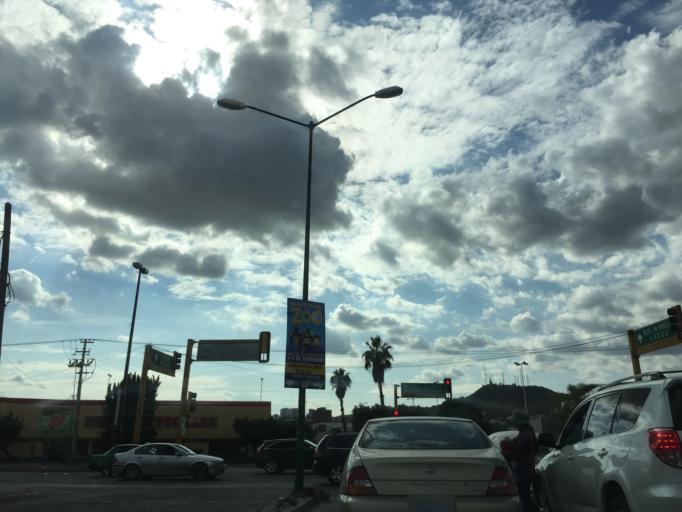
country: MX
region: Guanajuato
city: Leon
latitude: 21.1602
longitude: -101.6919
